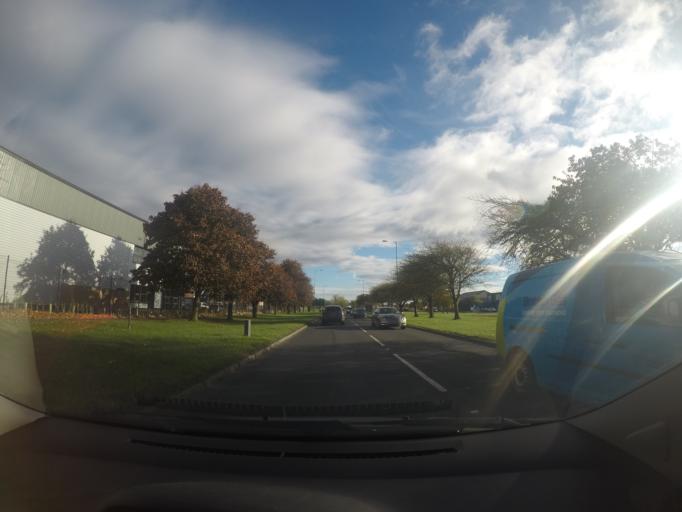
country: GB
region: England
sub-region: City and Borough of Leeds
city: Shadwell
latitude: 53.8288
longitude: -1.4603
